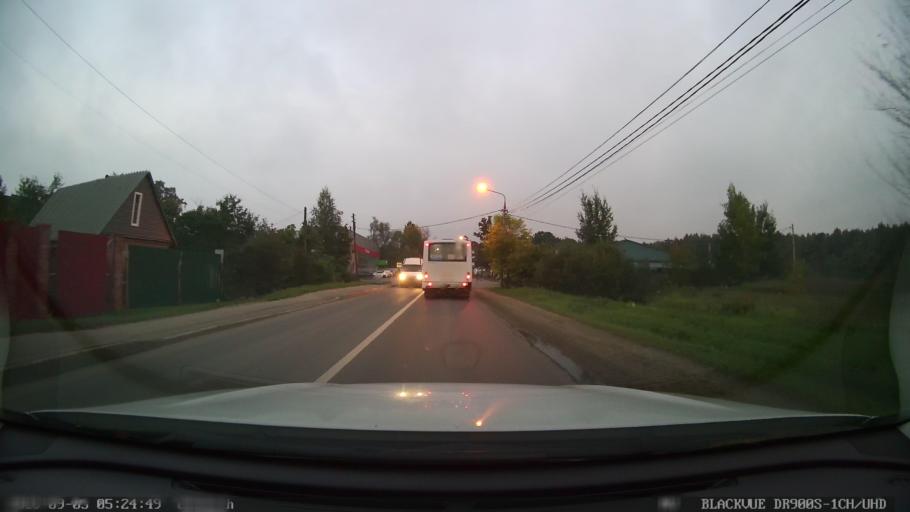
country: RU
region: Moskovskaya
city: Levoberezhnaya
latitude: 55.9188
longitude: 37.4695
